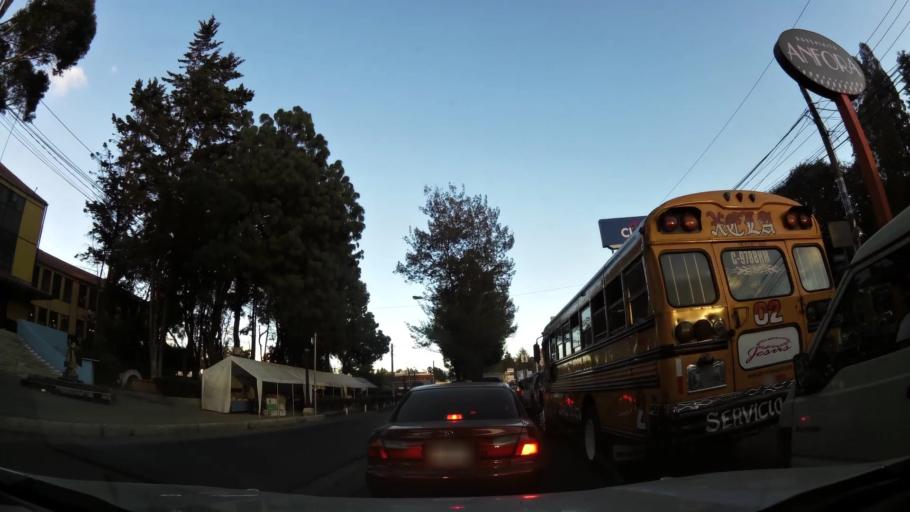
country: GT
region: Quetzaltenango
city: Quetzaltenango
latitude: 14.8448
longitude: -91.5243
